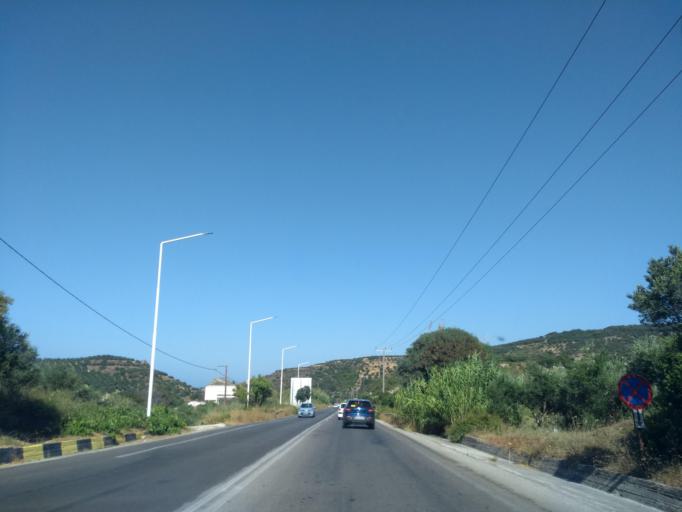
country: GR
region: Crete
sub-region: Nomos Chanias
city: Kolympari
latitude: 35.5283
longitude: 23.7532
